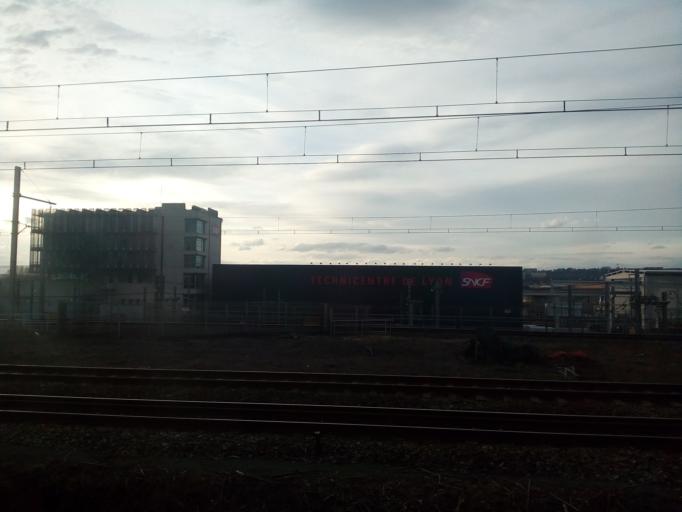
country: FR
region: Rhone-Alpes
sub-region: Departement du Rhone
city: Lyon
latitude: 45.7349
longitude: 4.8502
